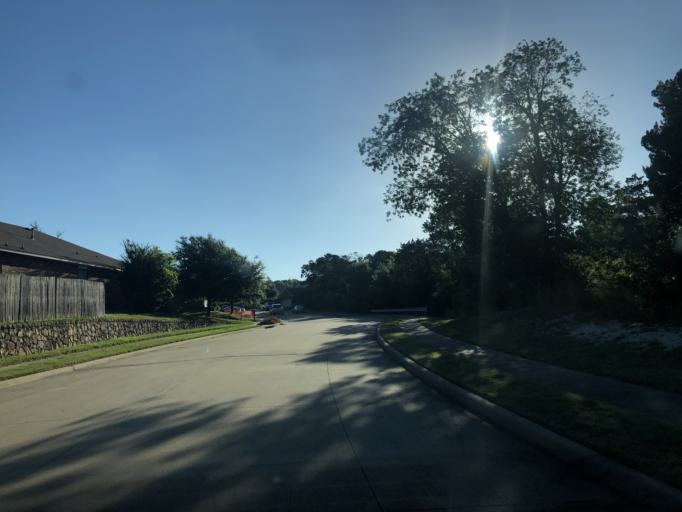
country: US
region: Texas
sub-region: Dallas County
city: Duncanville
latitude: 32.6555
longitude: -96.9457
